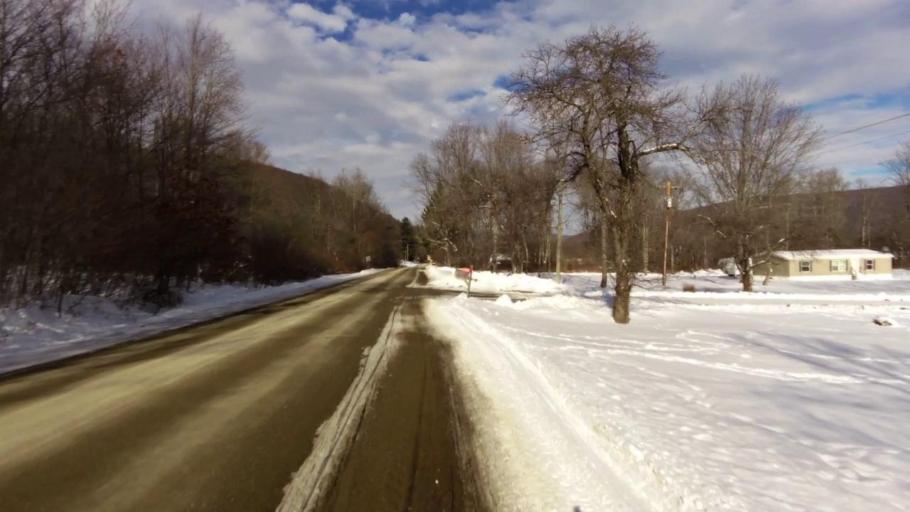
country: US
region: Pennsylvania
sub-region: McKean County
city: Foster Brook
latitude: 42.0636
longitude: -78.6466
